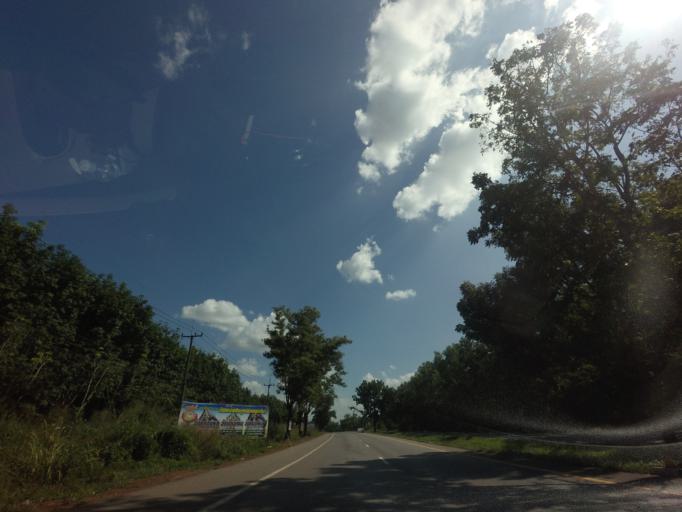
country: TH
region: Rayong
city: Wang Chan
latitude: 12.9721
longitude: 101.4948
